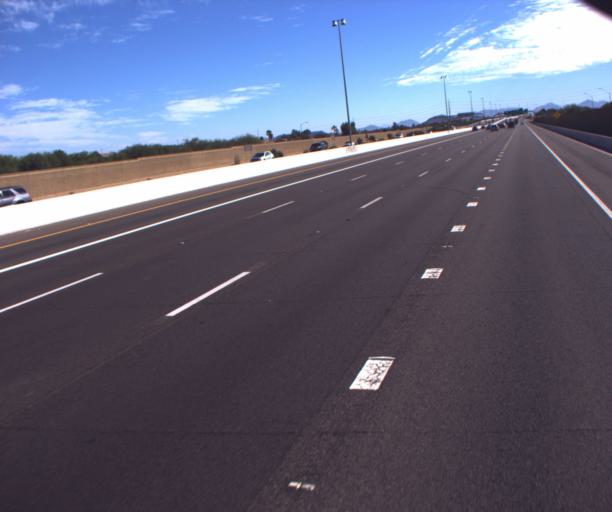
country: US
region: Arizona
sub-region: Maricopa County
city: Peoria
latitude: 33.6694
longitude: -112.1451
